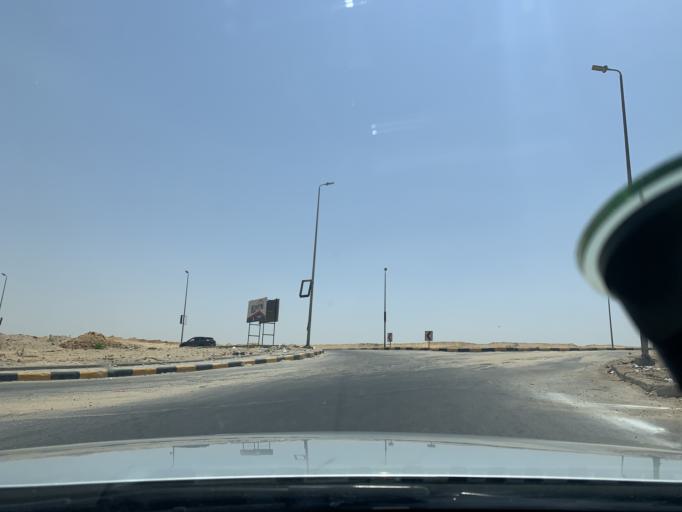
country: EG
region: Muhafazat al Qahirah
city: Cairo
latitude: 30.0000
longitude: 31.4628
